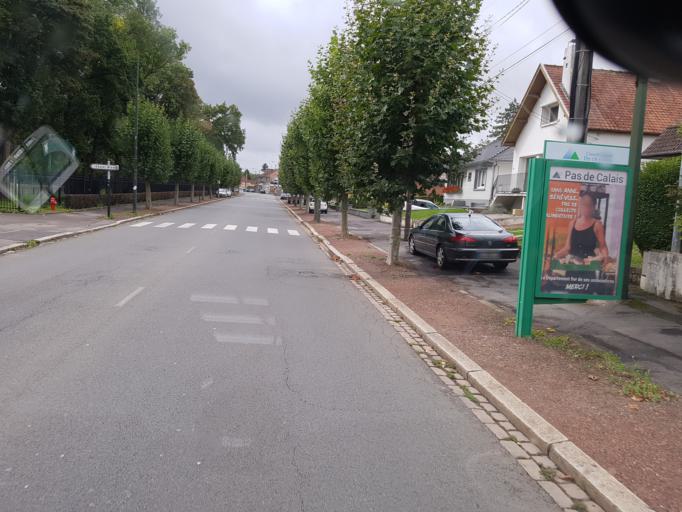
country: FR
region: Nord-Pas-de-Calais
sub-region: Departement du Pas-de-Calais
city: Angres
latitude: 50.4146
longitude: 2.7632
